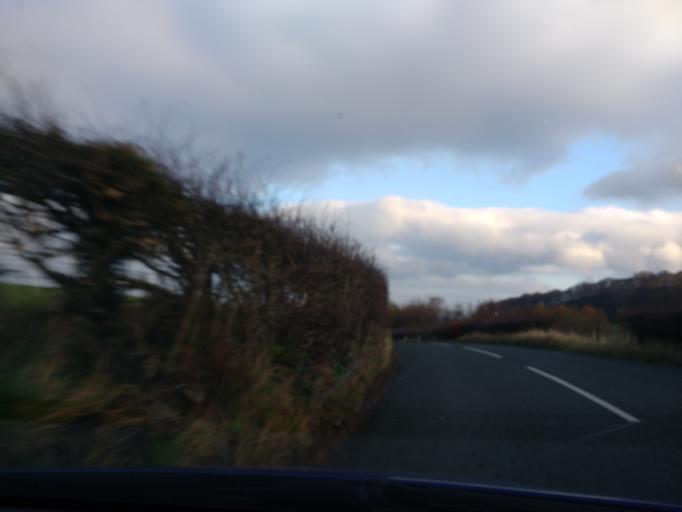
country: GB
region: England
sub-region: Lancashire
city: Caton
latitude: 54.0573
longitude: -2.7279
